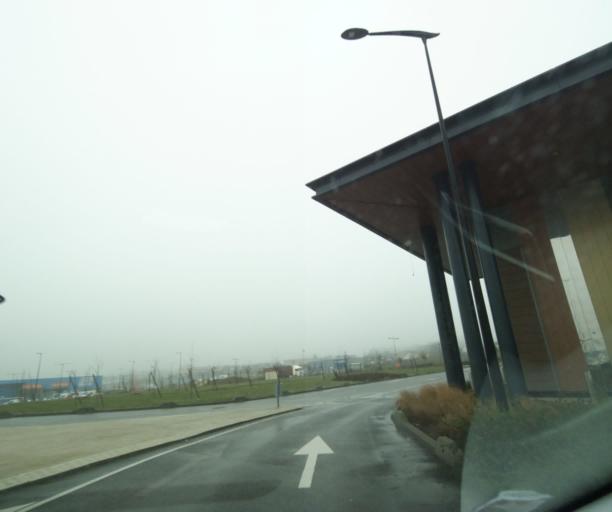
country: FR
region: Ile-de-France
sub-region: Departement de Seine-et-Marne
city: Saint-Mard
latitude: 49.0347
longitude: 2.6819
